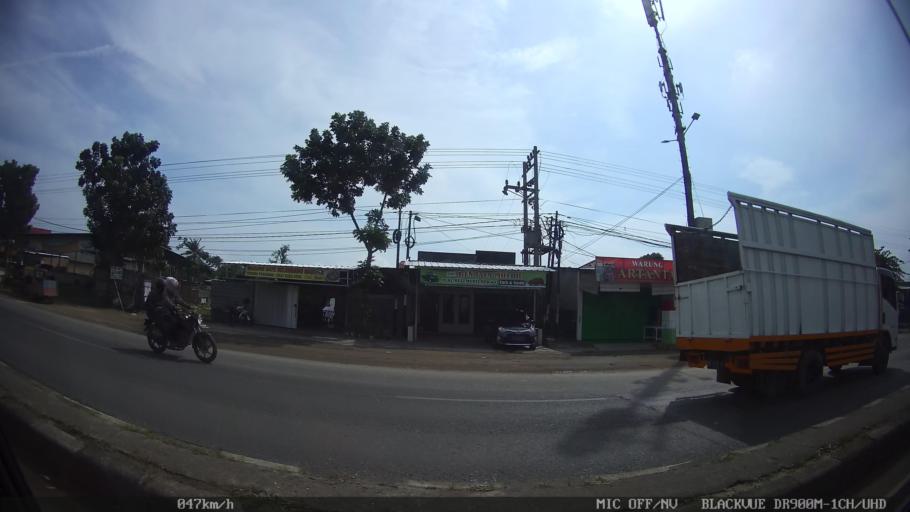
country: ID
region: Lampung
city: Kedaton
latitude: -5.3741
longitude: 105.2777
